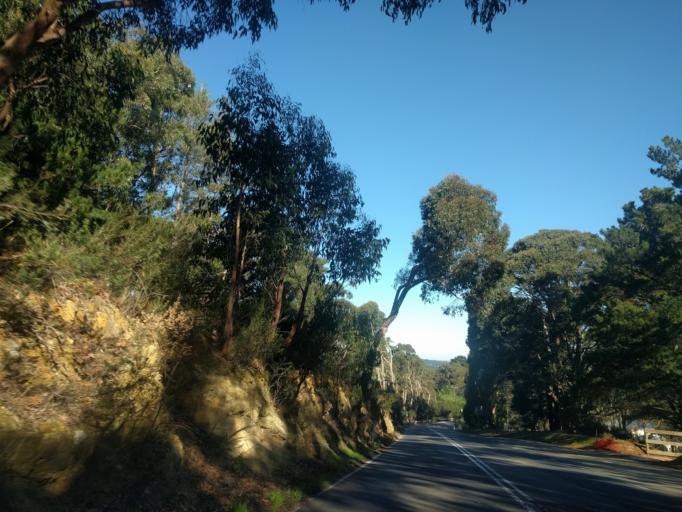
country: AU
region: South Australia
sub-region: Adelaide Hills
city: Crafers
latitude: -35.0116
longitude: 138.6985
